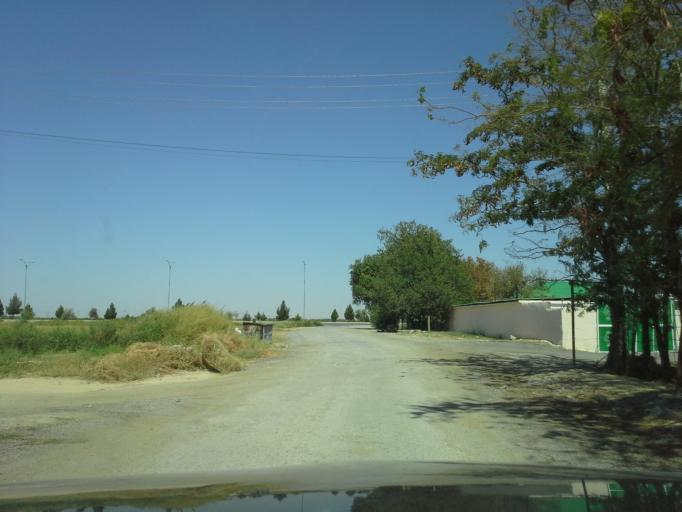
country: TM
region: Ahal
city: Ashgabat
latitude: 37.9983
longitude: 58.3203
